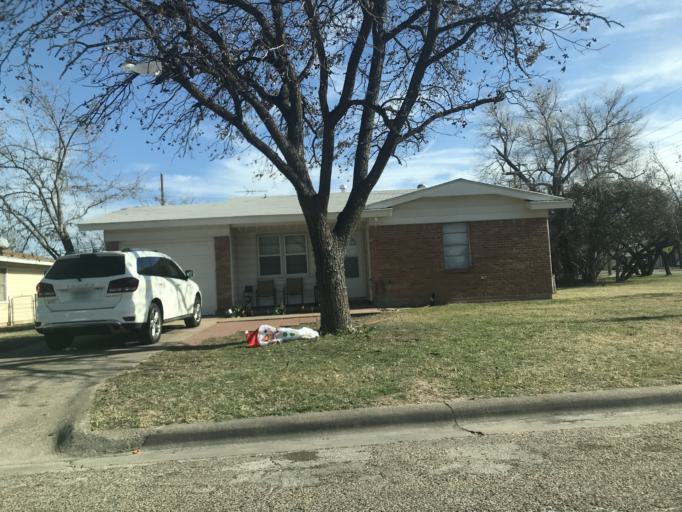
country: US
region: Texas
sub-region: Taylor County
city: Abilene
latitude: 32.4177
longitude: -99.7585
